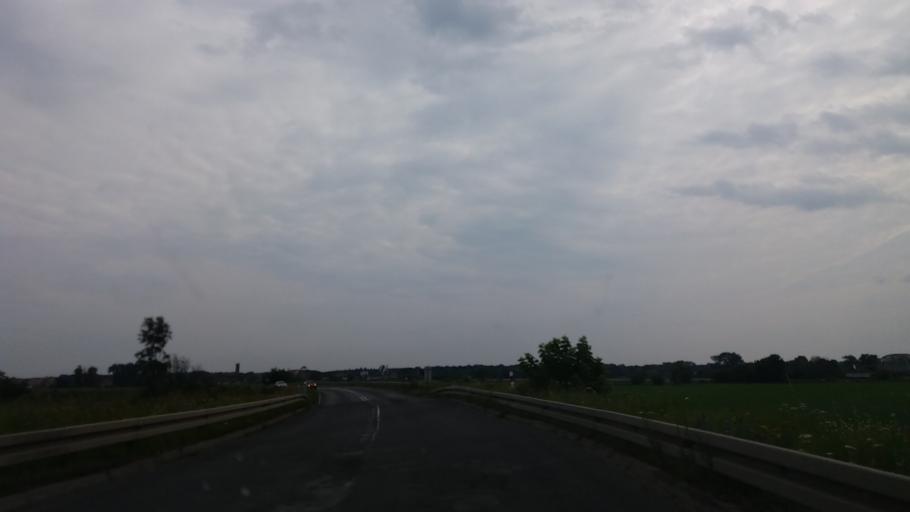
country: PL
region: Lubusz
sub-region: Powiat miedzyrzecki
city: Skwierzyna
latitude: 52.6060
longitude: 15.4853
